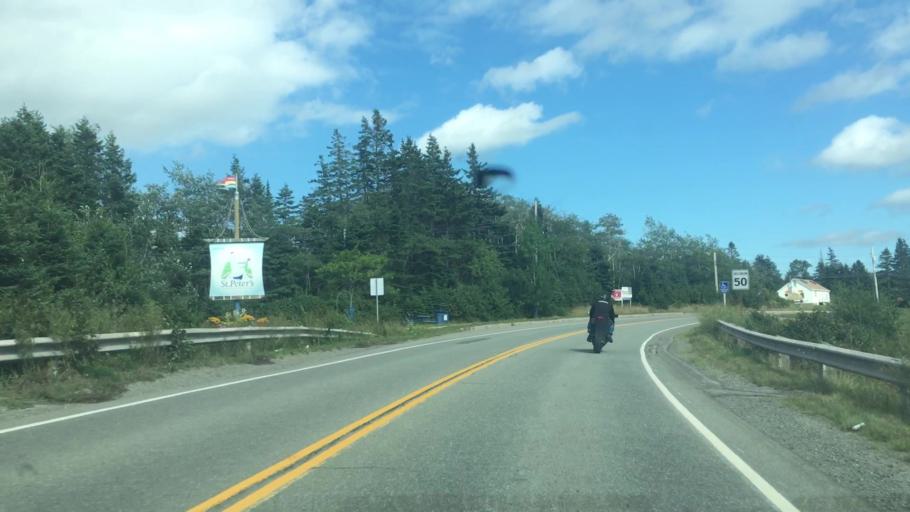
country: CA
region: Nova Scotia
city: Princeville
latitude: 45.6556
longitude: -60.8966
